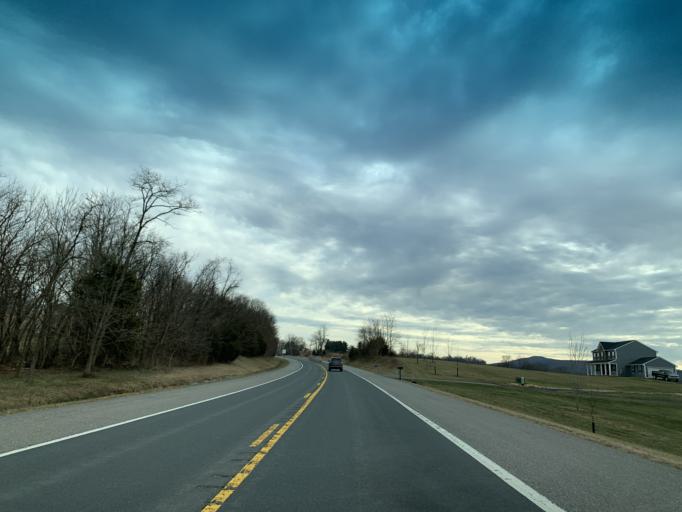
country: US
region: Maryland
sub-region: Washington County
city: Keedysville
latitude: 39.4454
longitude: -77.6653
